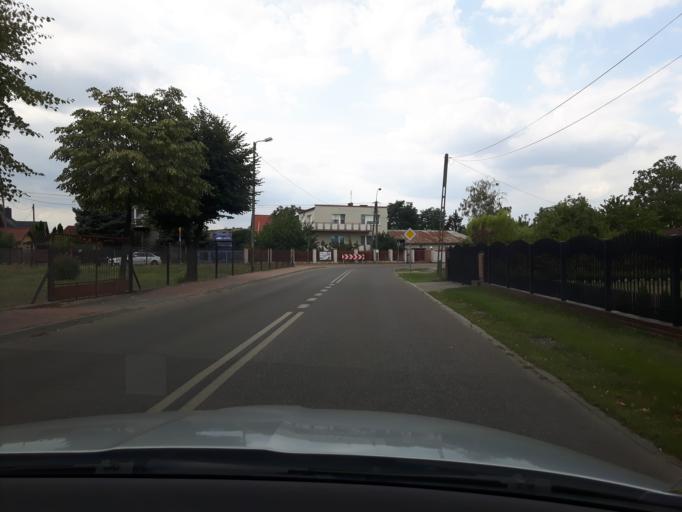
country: PL
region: Masovian Voivodeship
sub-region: Powiat legionowski
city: Wieliszew
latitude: 52.4524
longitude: 20.9648
